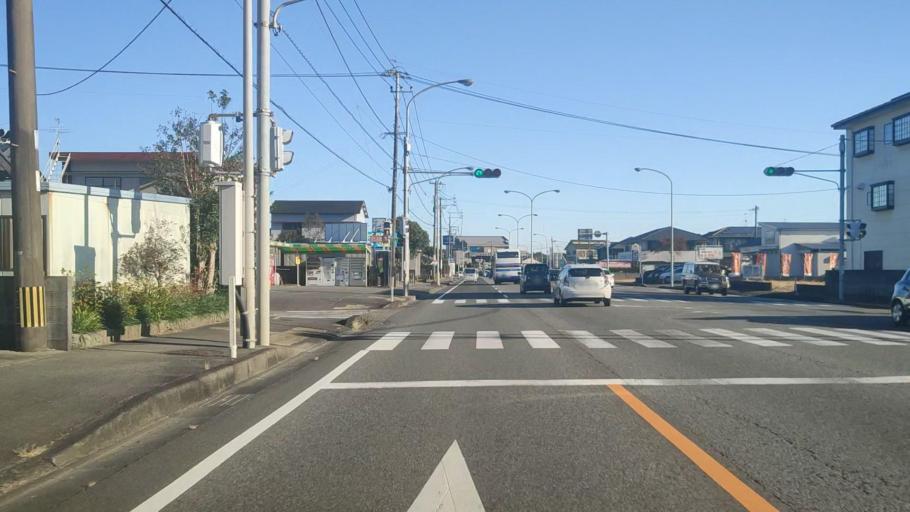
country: JP
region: Miyazaki
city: Nobeoka
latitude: 32.4599
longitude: 131.6470
